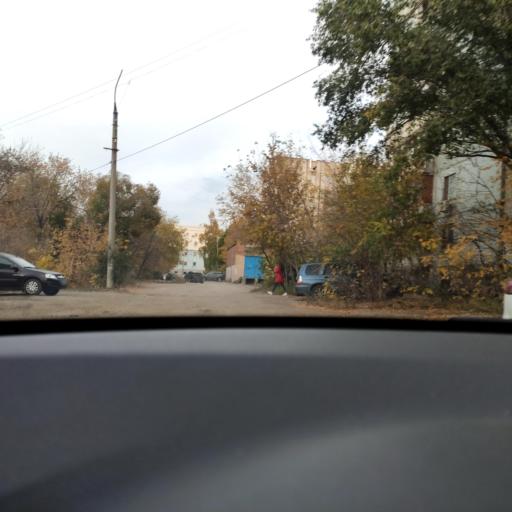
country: RU
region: Samara
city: Samara
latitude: 53.2019
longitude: 50.1478
